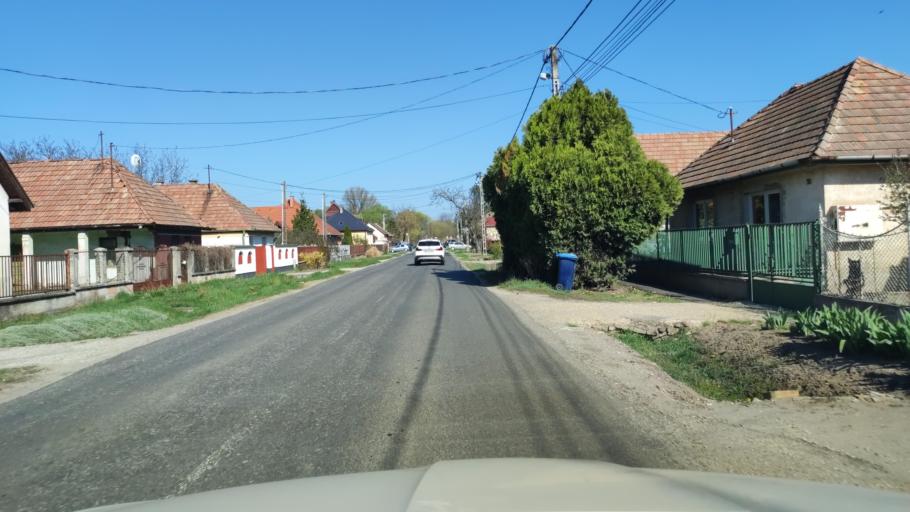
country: HU
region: Pest
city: Nagytarcsa
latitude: 47.5329
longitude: 19.2802
